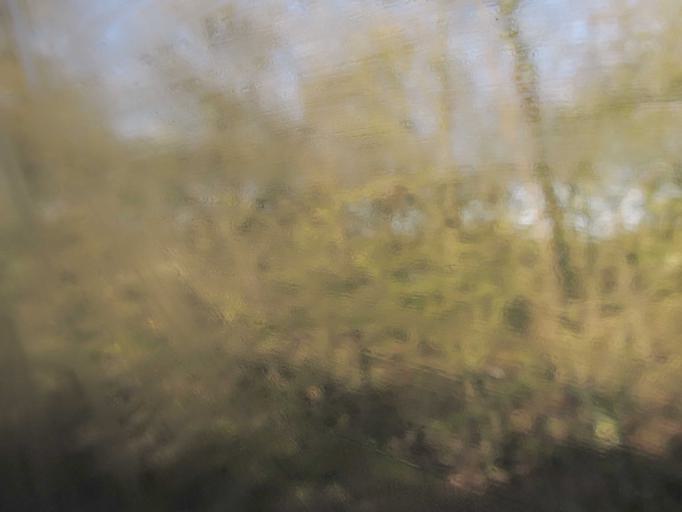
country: GB
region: England
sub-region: Hampshire
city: Kings Worthy
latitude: 51.1637
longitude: -1.3191
